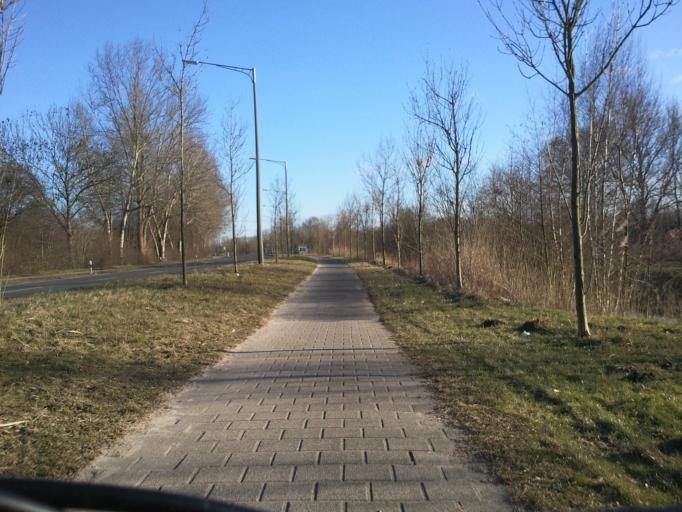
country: DE
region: Lower Saxony
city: Stuhr
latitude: 53.0771
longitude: 8.7594
